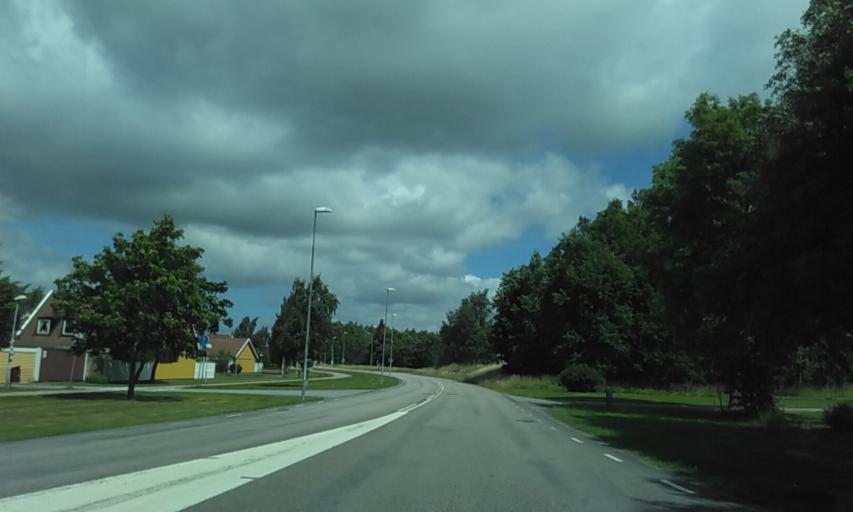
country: SE
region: Vaestra Goetaland
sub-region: Grastorps Kommun
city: Graestorp
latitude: 58.3307
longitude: 12.6904
